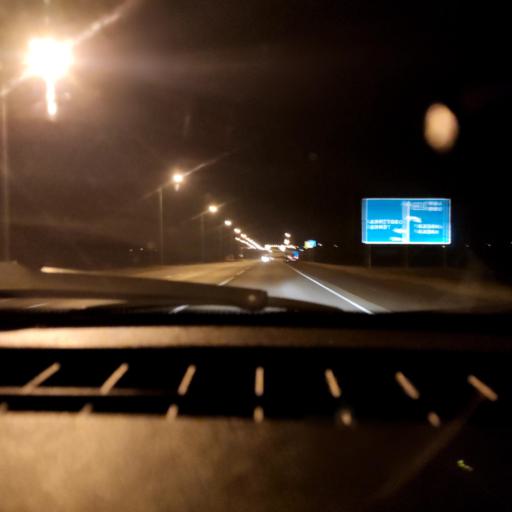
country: RU
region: Bashkortostan
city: Kushnarenkovo
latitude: 55.0679
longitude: 55.4163
